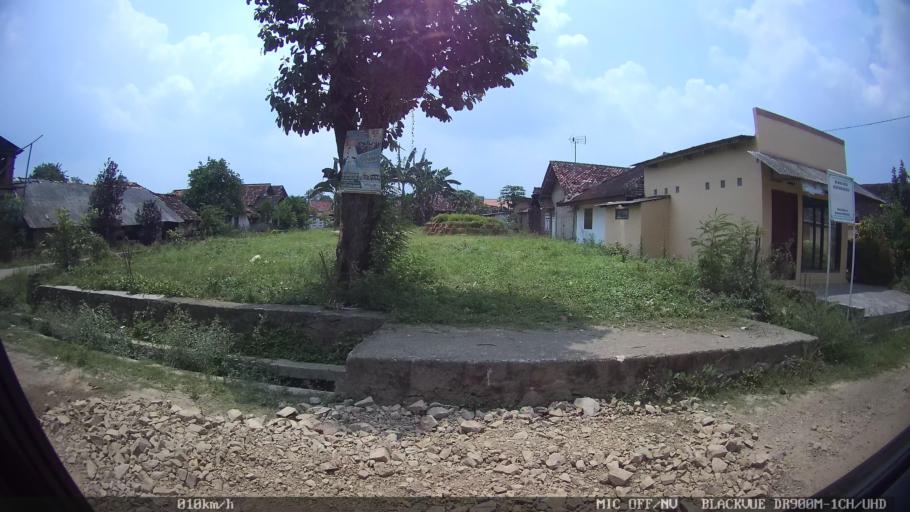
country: ID
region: Lampung
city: Pringsewu
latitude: -5.3660
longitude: 105.0003
